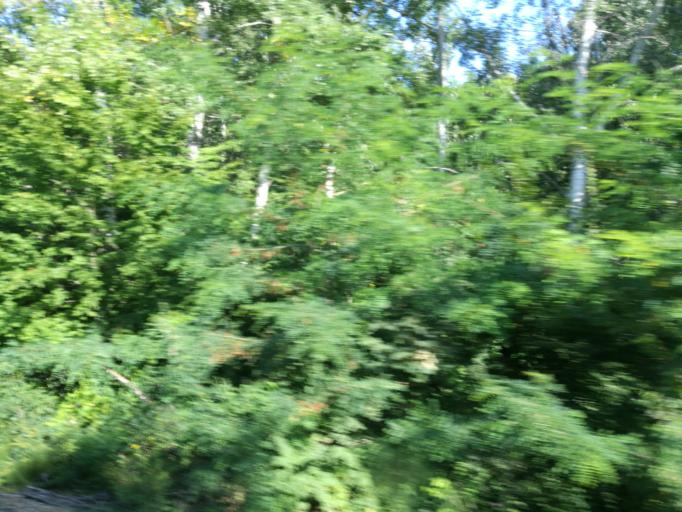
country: RO
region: Iasi
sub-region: Comuna Ciurea
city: Ciurea
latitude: 47.0196
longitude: 27.5805
